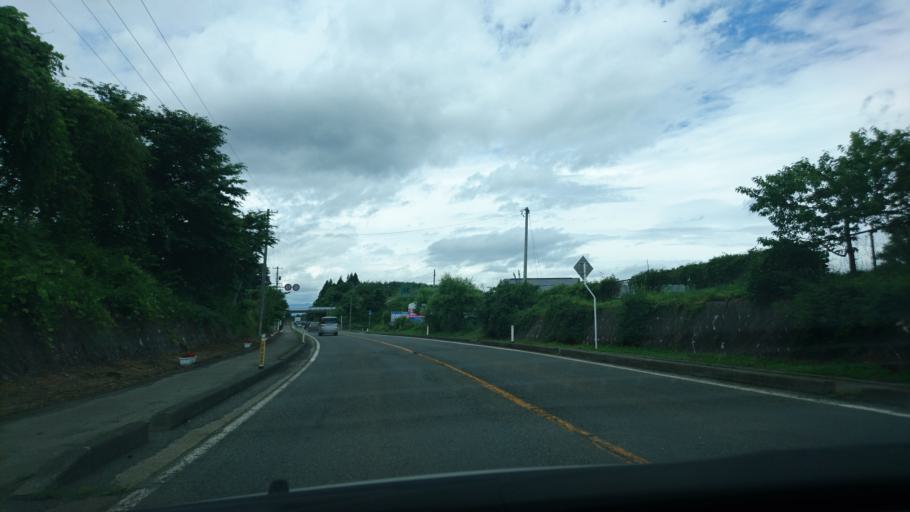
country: JP
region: Iwate
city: Morioka-shi
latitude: 39.6109
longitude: 141.2023
